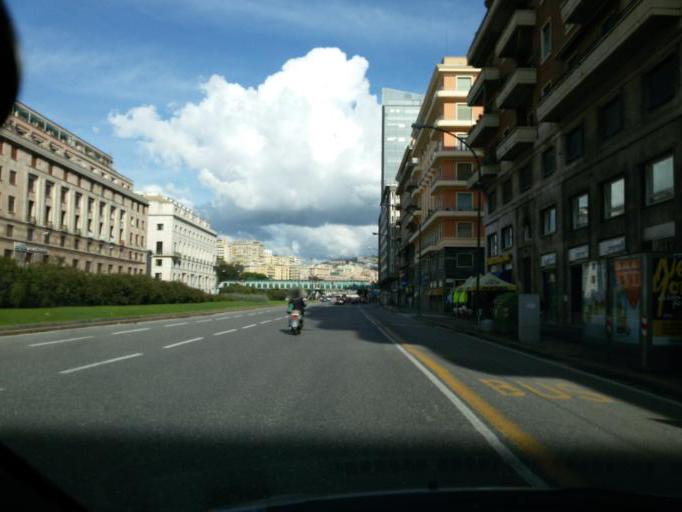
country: IT
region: Liguria
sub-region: Provincia di Genova
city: San Teodoro
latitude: 44.4021
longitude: 8.9465
